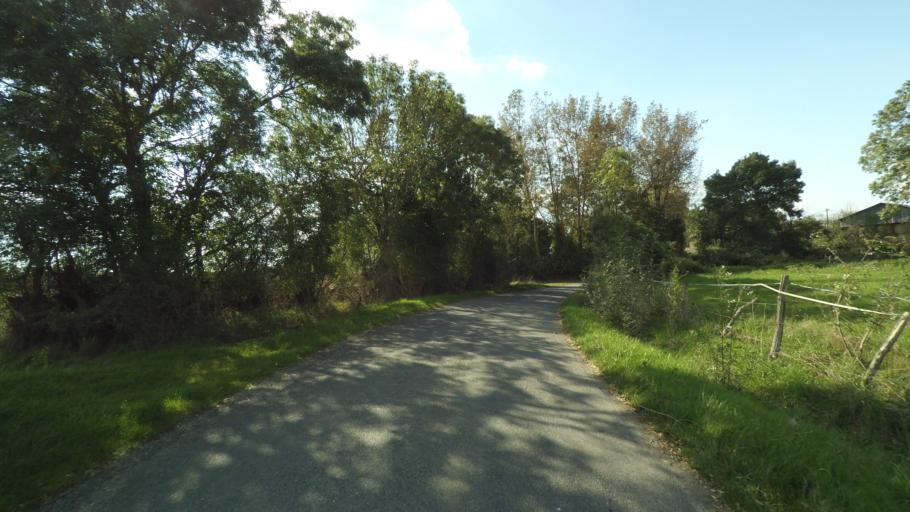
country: FR
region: Pays de la Loire
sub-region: Departement de la Loire-Atlantique
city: Vieillevigne
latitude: 46.9746
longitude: -1.4081
